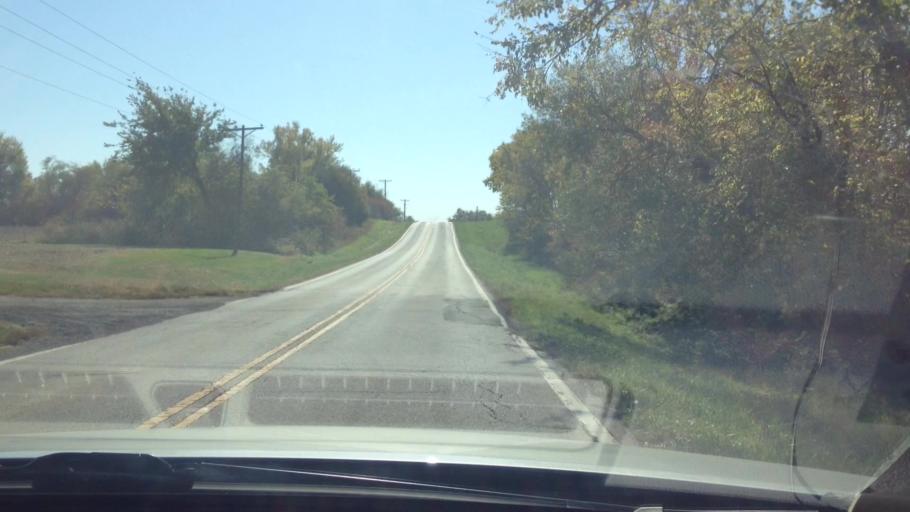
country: US
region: Missouri
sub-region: Clay County
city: Smithville
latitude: 39.3311
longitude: -94.6488
